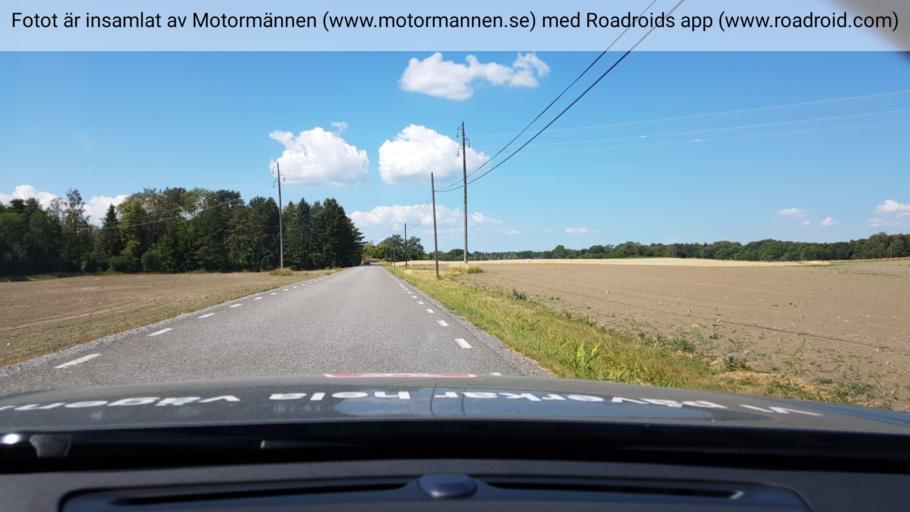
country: SE
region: Stockholm
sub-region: Upplands-Bro Kommun
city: Kungsaengen
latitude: 59.4071
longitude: 17.7054
